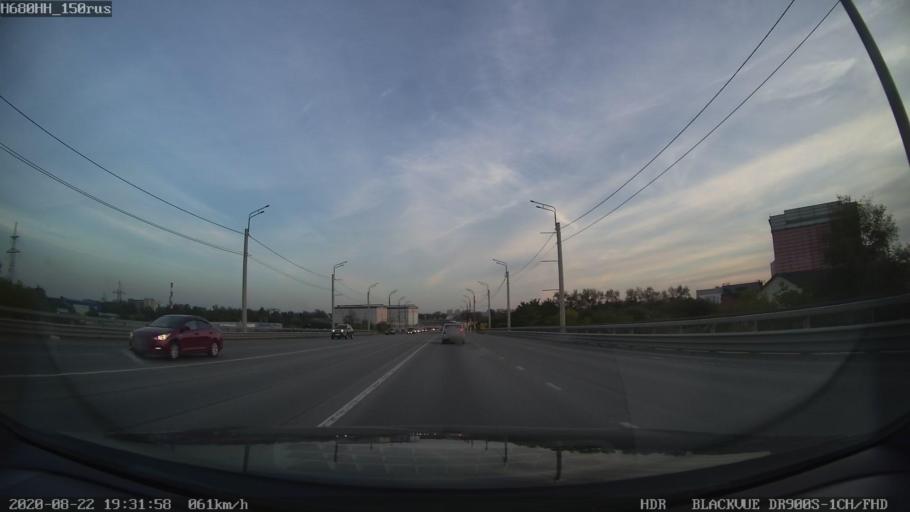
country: RU
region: Tverskaya
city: Tver
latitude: 56.8547
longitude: 35.9440
